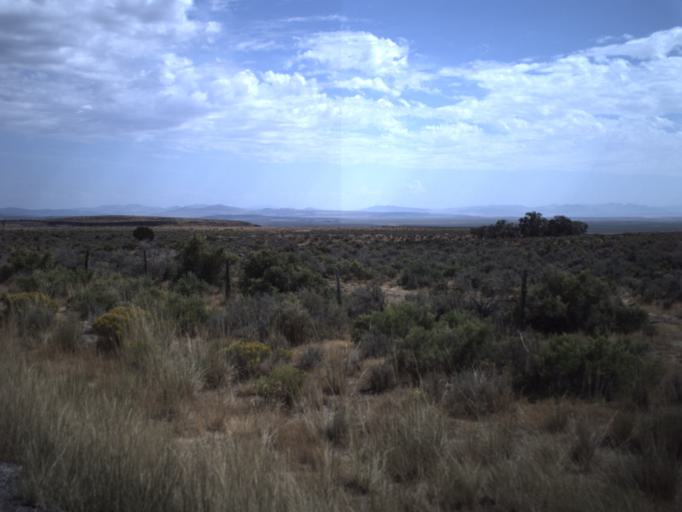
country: US
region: Idaho
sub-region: Minidoka County
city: Heyburn
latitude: 41.8212
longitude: -113.1920
